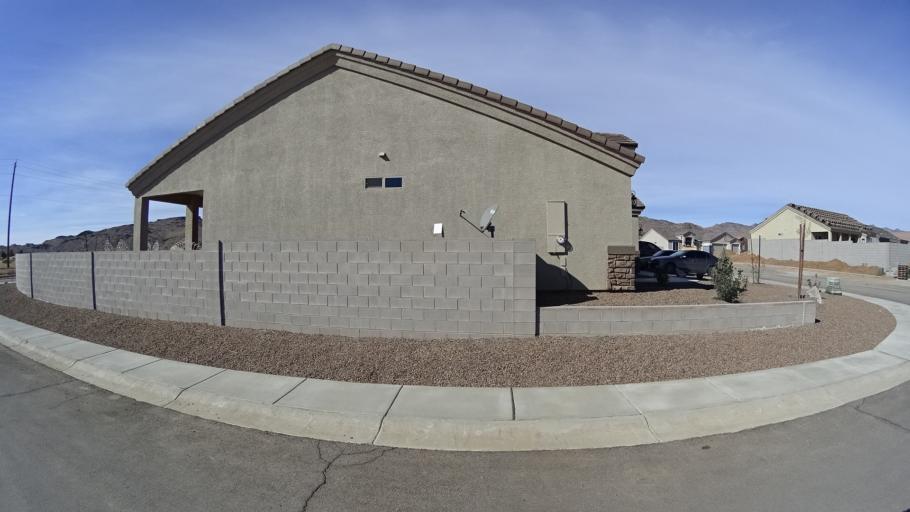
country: US
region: Arizona
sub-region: Mohave County
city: New Kingman-Butler
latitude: 35.2761
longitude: -114.0349
